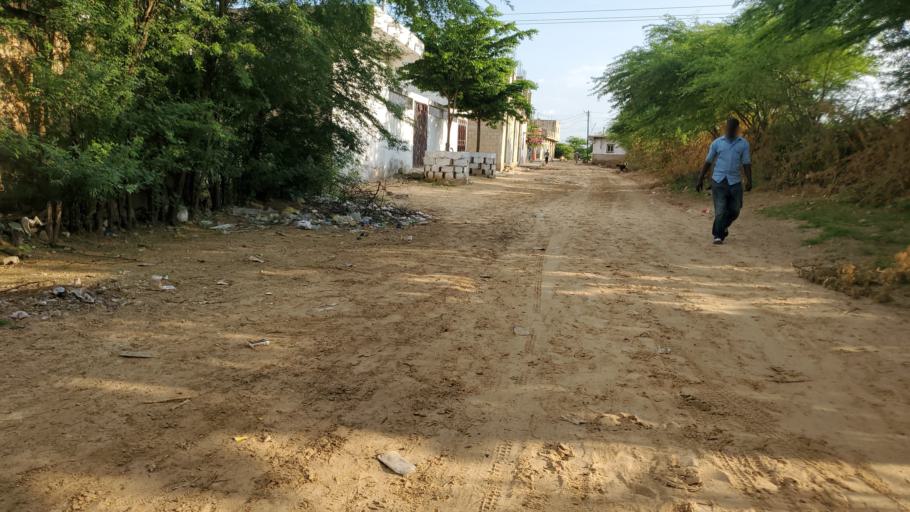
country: SN
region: Saint-Louis
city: Saint-Louis
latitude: 16.0604
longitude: -16.4188
